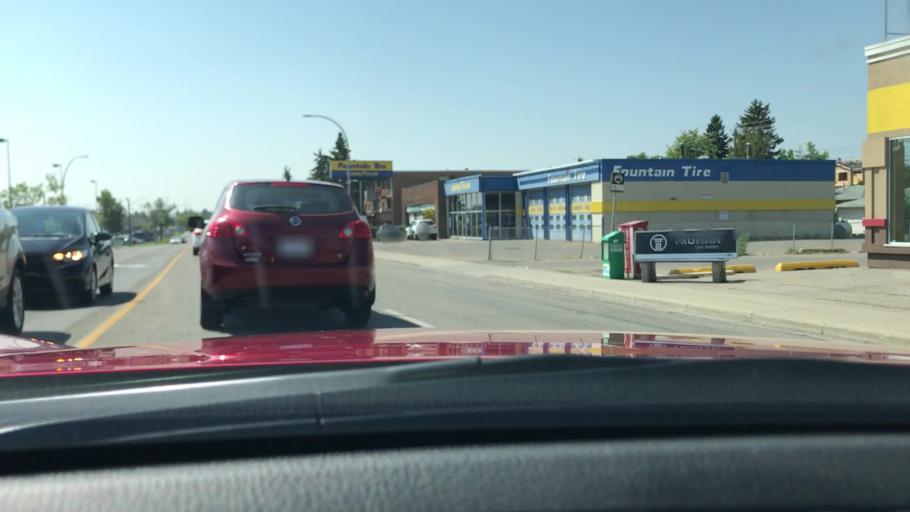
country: CA
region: Alberta
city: Calgary
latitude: 51.0449
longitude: -114.1412
